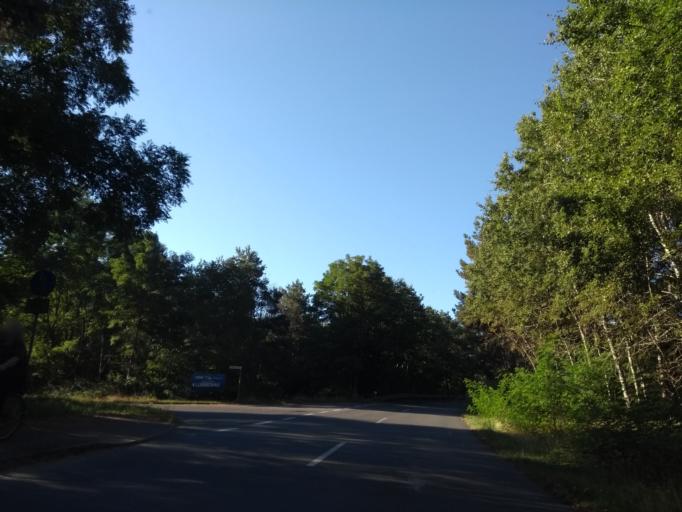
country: DE
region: Brandenburg
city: Lubbenau
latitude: 51.8411
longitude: 13.9508
